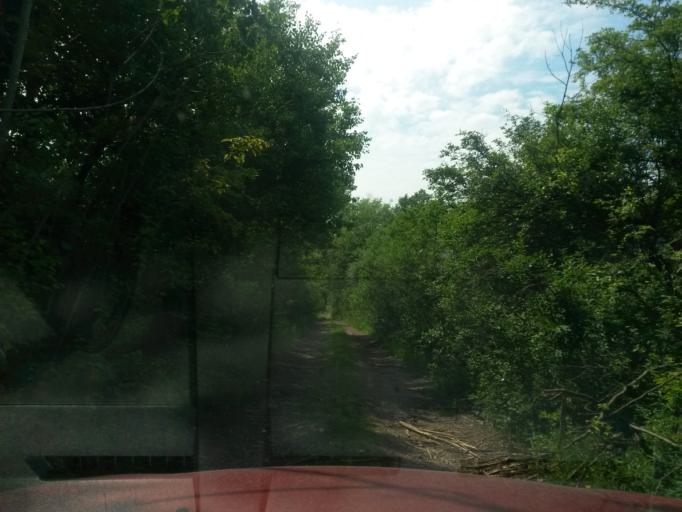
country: SK
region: Kosicky
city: Secovce
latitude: 48.6280
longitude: 21.4945
